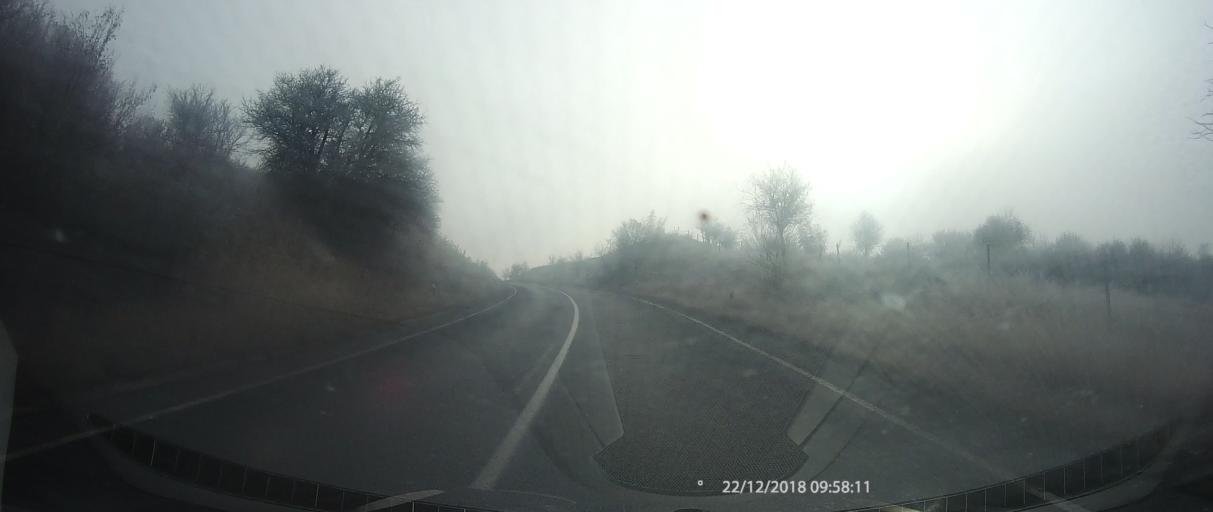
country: MK
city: Klechovce
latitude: 42.1569
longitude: 21.9364
